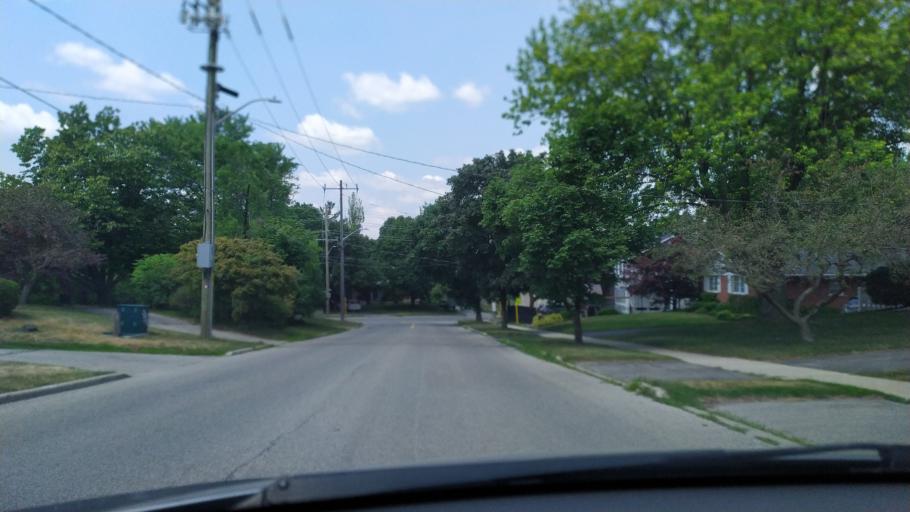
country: CA
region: Ontario
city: Waterloo
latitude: 43.4779
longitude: -80.5076
